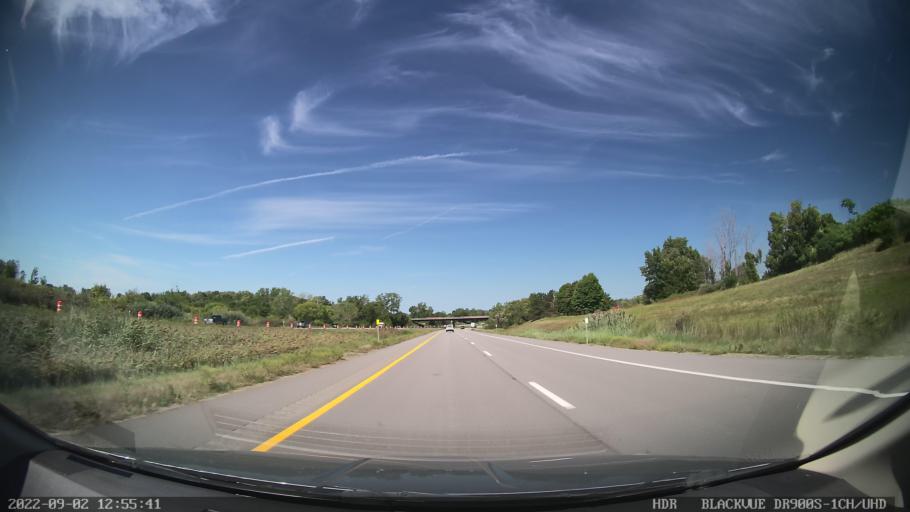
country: US
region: New York
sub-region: Livingston County
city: Avon
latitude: 42.9448
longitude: -77.6940
